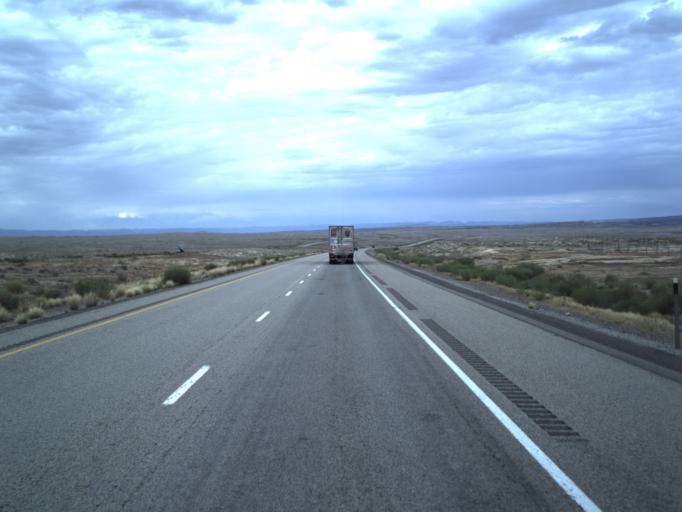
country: US
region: Utah
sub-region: Grand County
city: Moab
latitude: 38.9573
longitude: -109.3836
